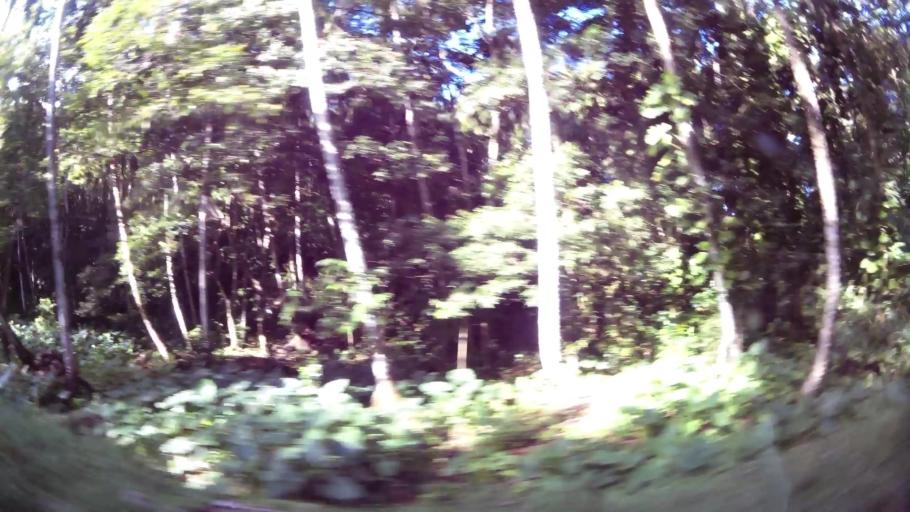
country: DM
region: Saint Andrew
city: Calibishie
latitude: 15.5923
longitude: -61.3621
